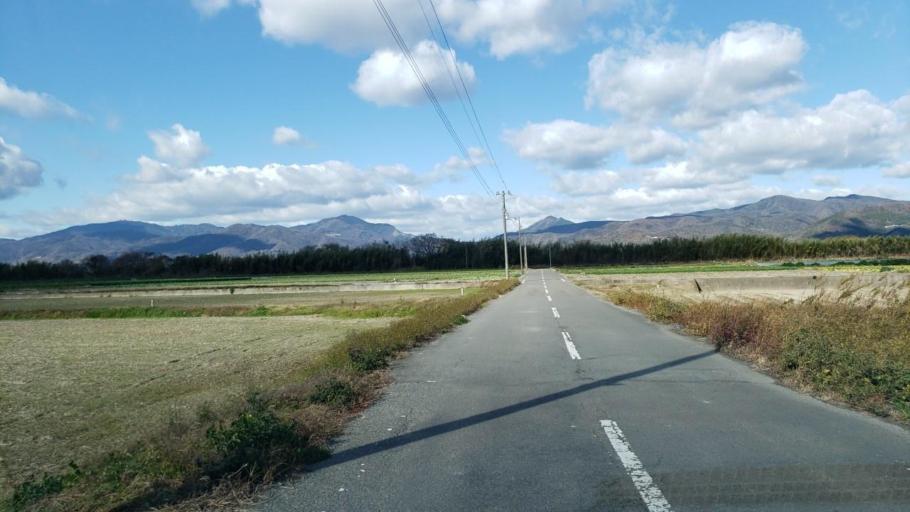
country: JP
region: Tokushima
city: Kamojimacho-jogejima
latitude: 34.0731
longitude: 134.2995
